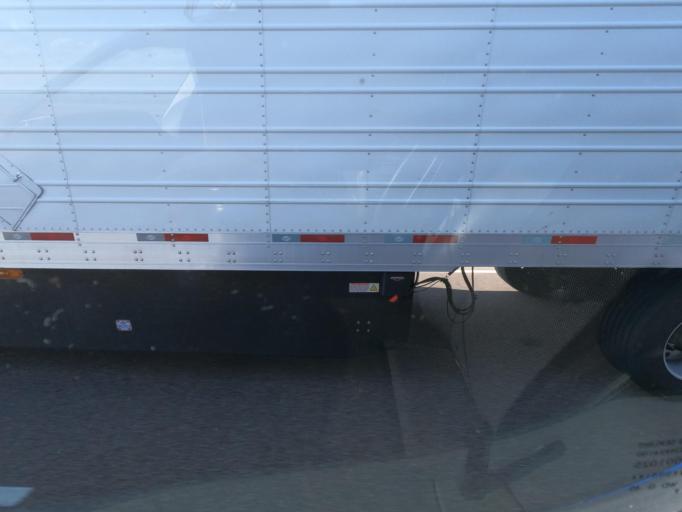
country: US
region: Wyoming
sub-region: Uinta County
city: Lyman
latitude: 41.3595
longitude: -110.3301
